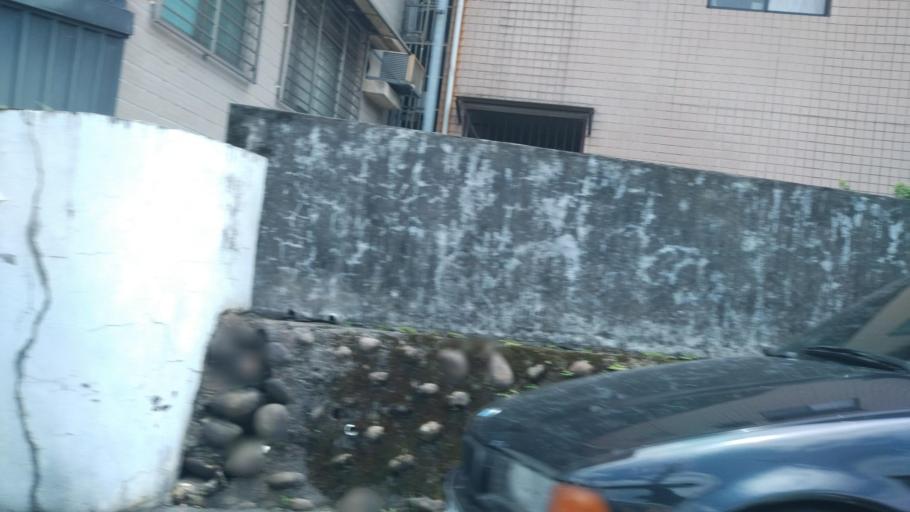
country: TW
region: Taipei
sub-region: Taipei
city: Banqiao
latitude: 24.9495
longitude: 121.4892
